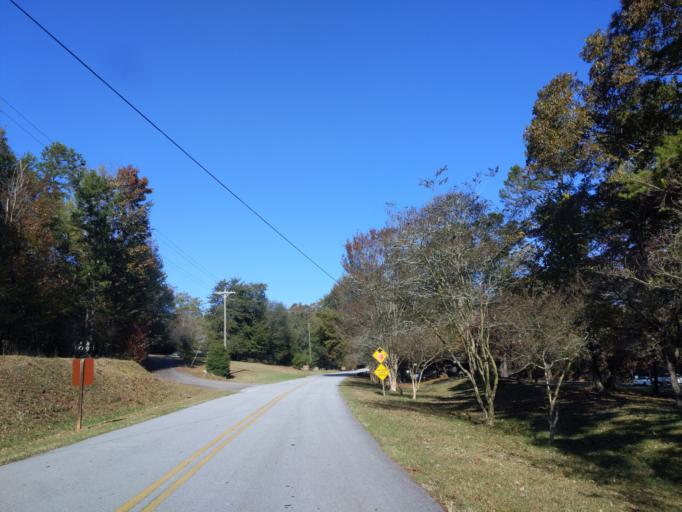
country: US
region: Georgia
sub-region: Franklin County
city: Gumlog
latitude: 34.4967
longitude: -83.0766
